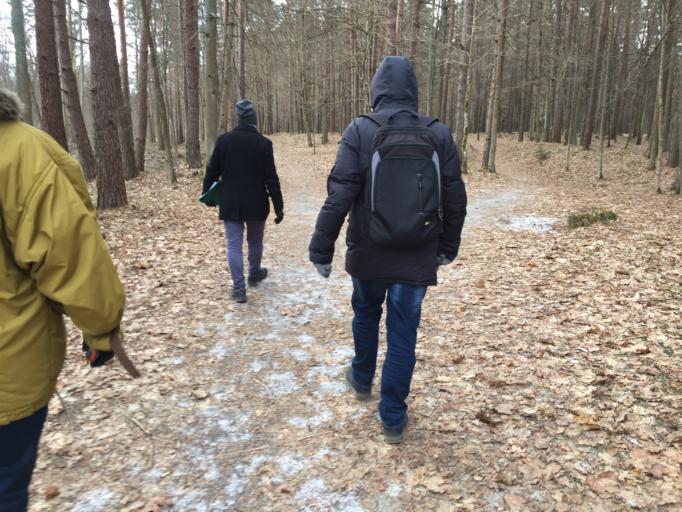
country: LV
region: Valmieras Rajons
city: Valmiera
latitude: 57.5367
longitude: 25.4439
